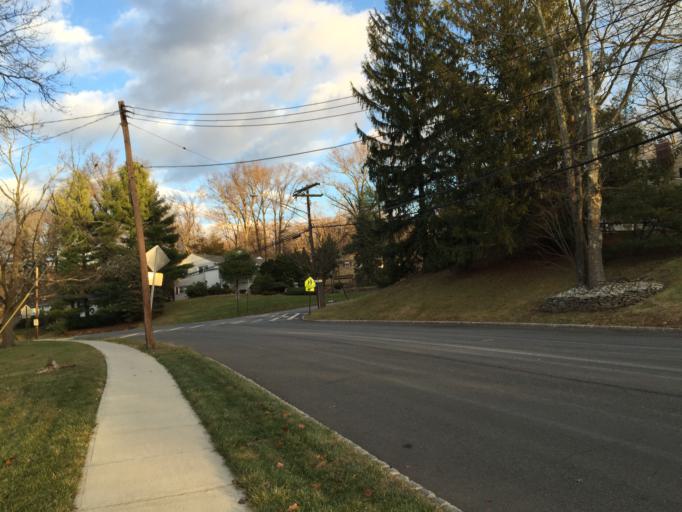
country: US
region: New Jersey
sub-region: Union County
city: New Providence
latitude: 40.7004
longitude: -74.3888
